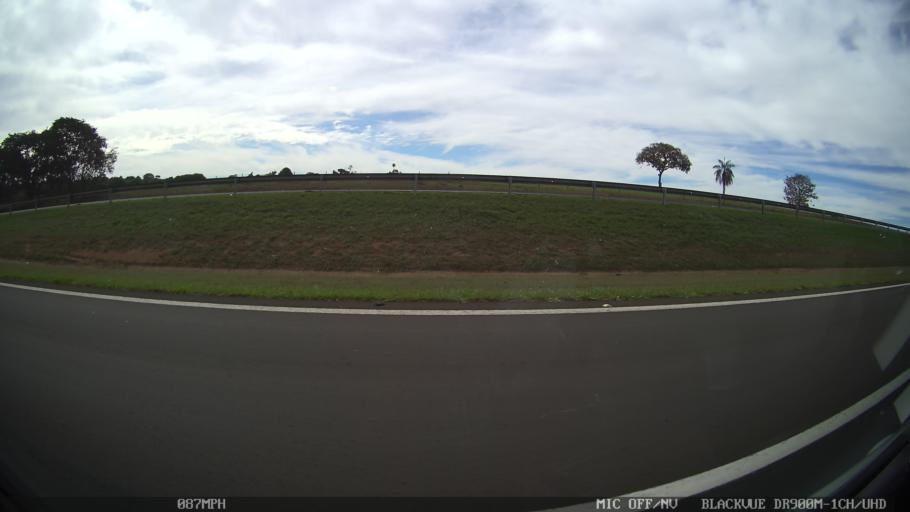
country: BR
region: Sao Paulo
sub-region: Taquaritinga
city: Taquaritinga
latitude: -21.4798
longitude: -48.5928
